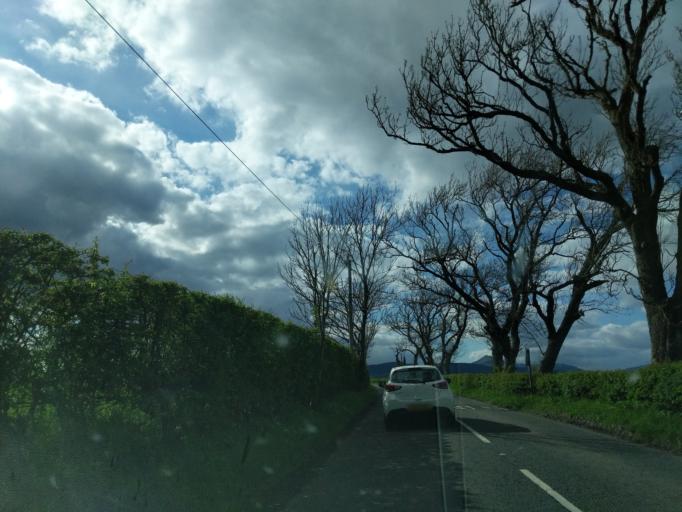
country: GB
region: Scotland
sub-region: Stirling
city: Doune
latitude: 56.1450
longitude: -4.1468
